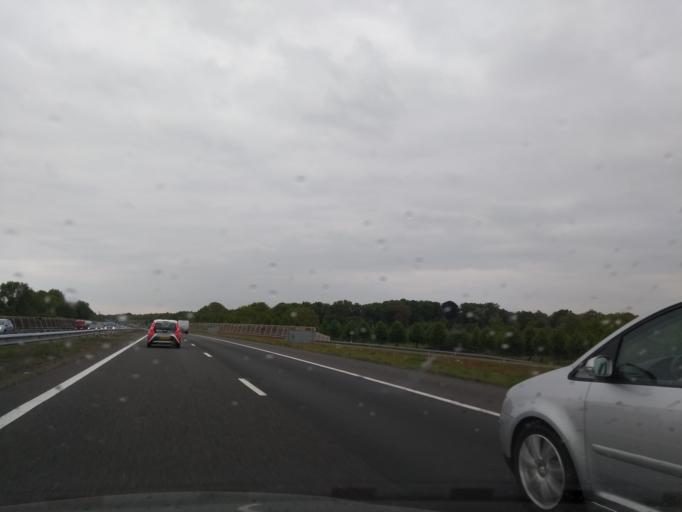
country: NL
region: Friesland
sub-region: Gemeente Heerenveen
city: Oranjewoud
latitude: 52.9421
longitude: 5.9517
